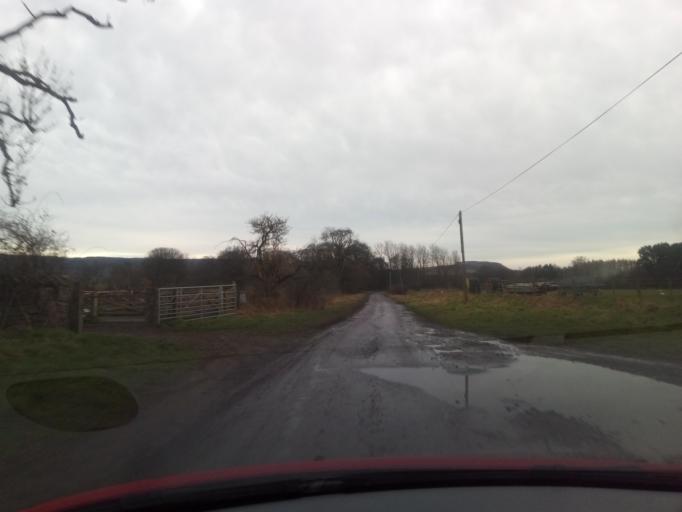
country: GB
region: England
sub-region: Northumberland
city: Wooler
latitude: 55.5064
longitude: -1.9308
